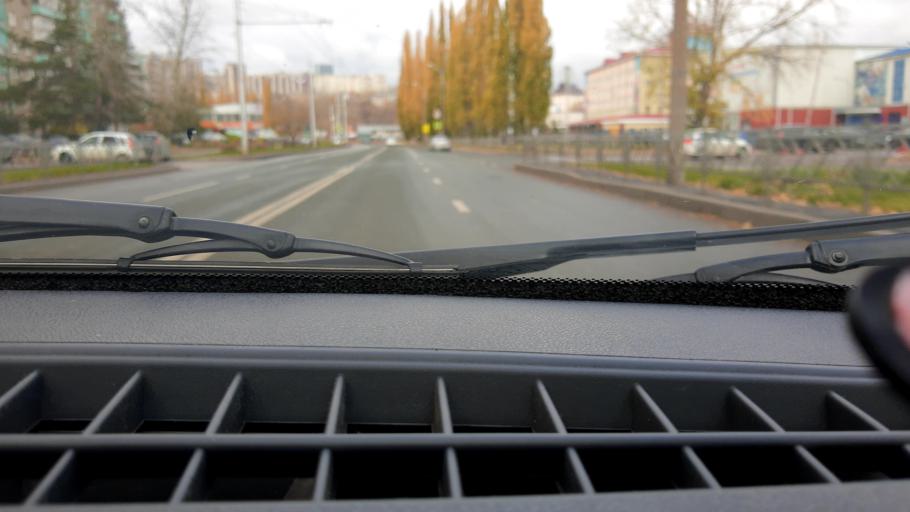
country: RU
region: Bashkortostan
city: Ufa
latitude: 54.7704
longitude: 56.0533
